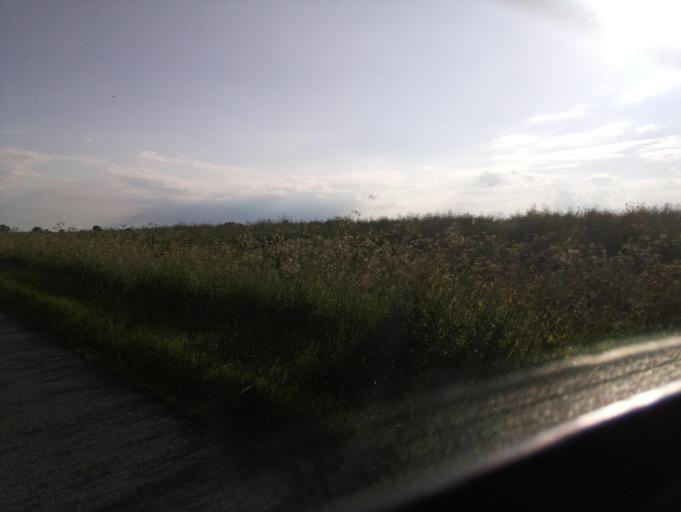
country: GB
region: England
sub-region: Lincolnshire
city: Navenby
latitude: 53.1108
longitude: -0.6004
